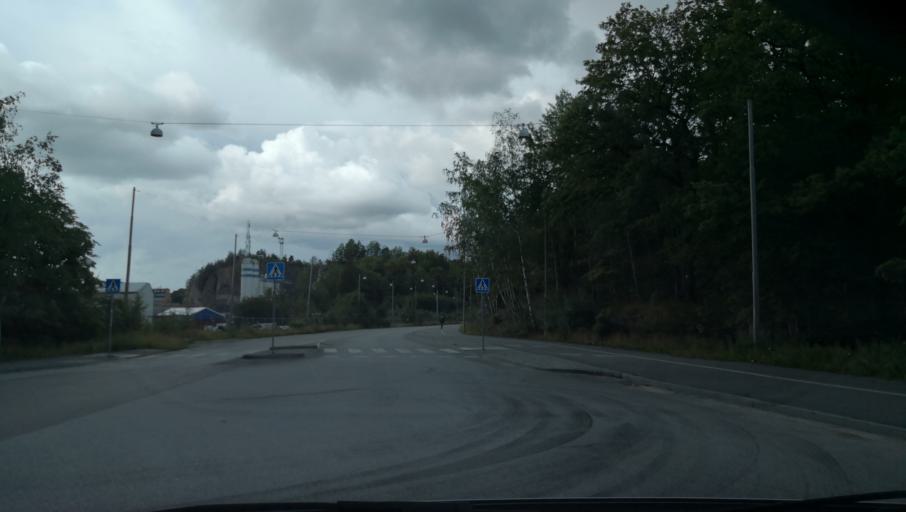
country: SE
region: Stockholm
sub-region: Haninge Kommun
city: Handen
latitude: 59.2352
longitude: 18.1199
